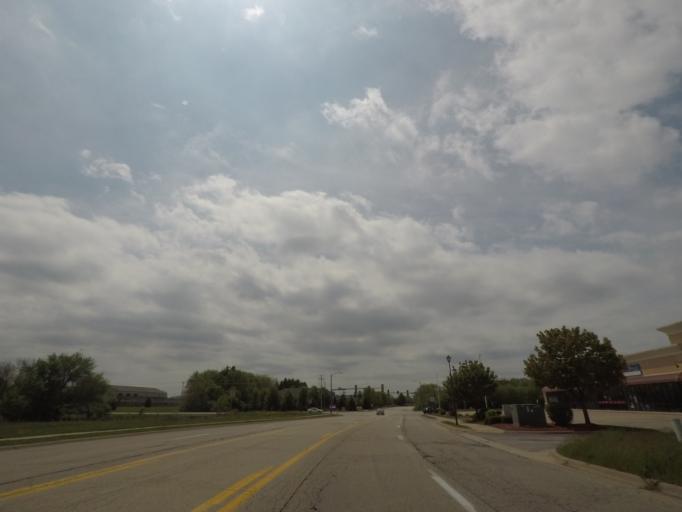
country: US
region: Illinois
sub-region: Winnebago County
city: Machesney Park
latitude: 42.3054
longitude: -88.9767
